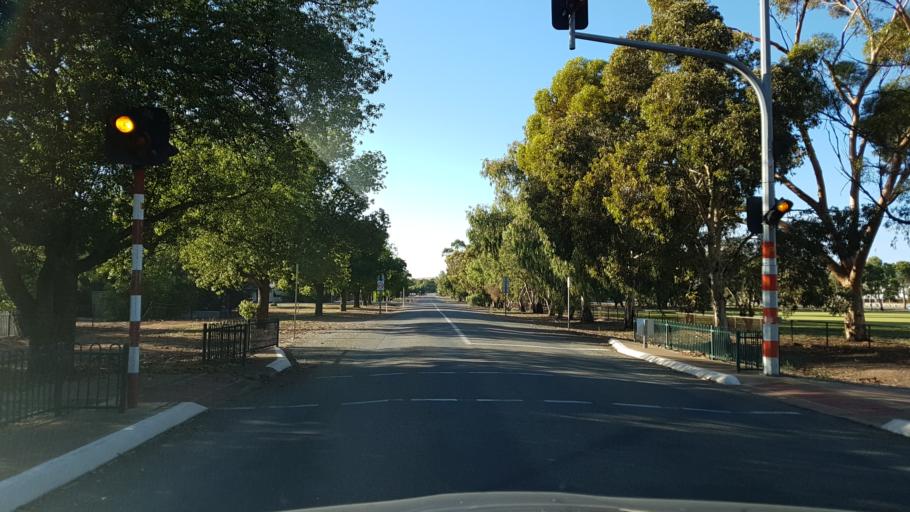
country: AU
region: South Australia
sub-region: Port Pirie City and Dists
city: Crystal Brook
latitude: -33.2725
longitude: 138.3536
